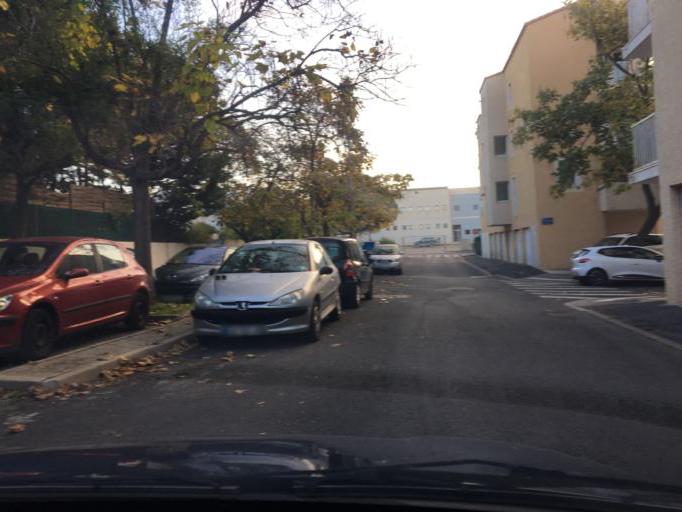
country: FR
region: Languedoc-Roussillon
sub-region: Departement de l'Herault
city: Castelnau-le-Lez
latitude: 43.6115
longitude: 3.9029
